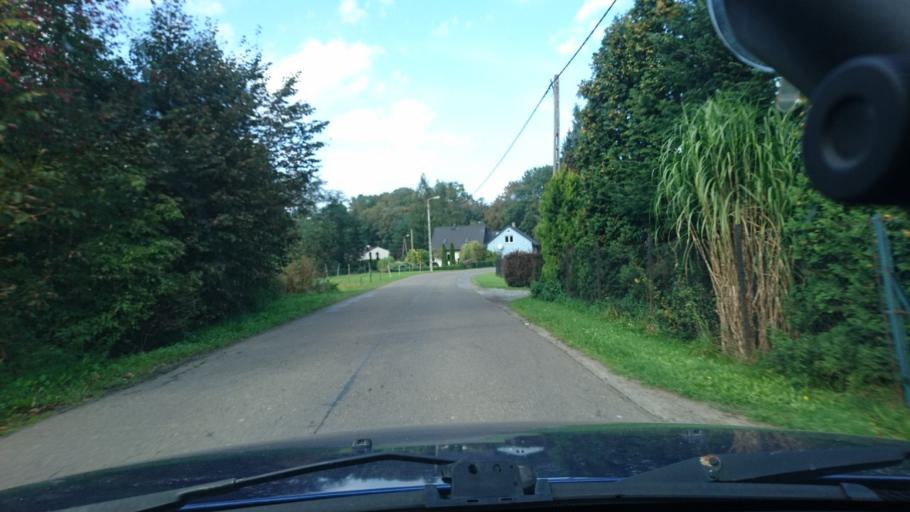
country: PL
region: Silesian Voivodeship
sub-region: Powiat bielski
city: Jasienica
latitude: 49.8189
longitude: 18.9203
